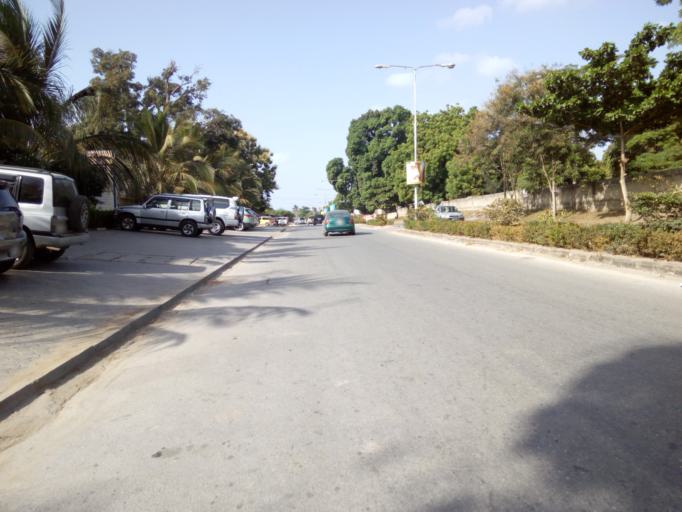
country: TZ
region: Zanzibar Urban/West
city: Zanzibar
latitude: -6.1738
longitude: 39.2016
